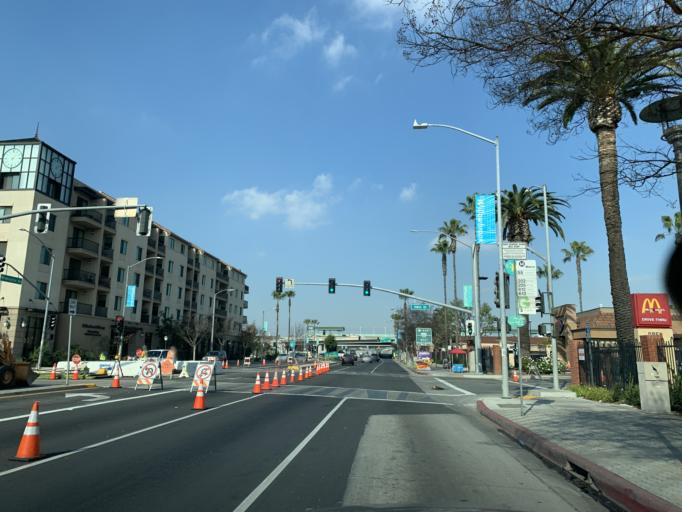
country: US
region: California
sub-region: Los Angeles County
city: Willowbrook
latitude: 33.9257
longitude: -118.2389
